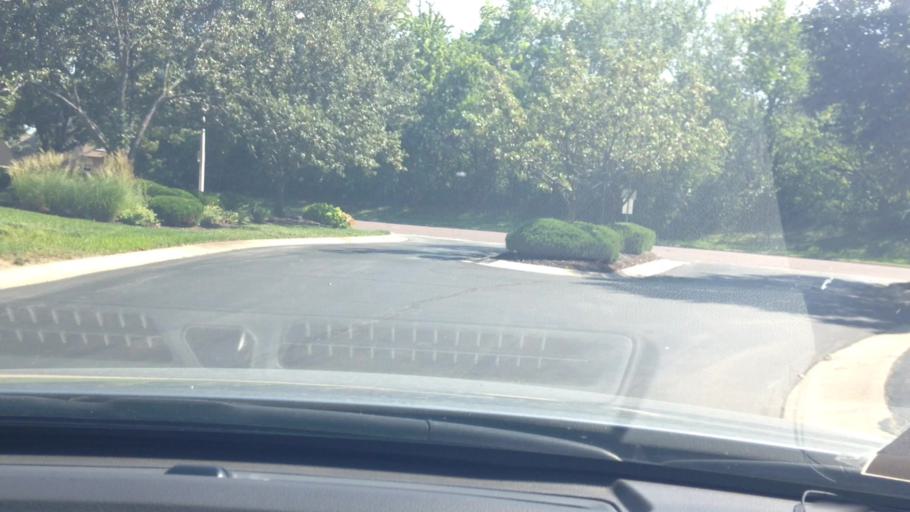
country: US
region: Kansas
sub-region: Johnson County
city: Lenexa
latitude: 38.8624
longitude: -94.6661
